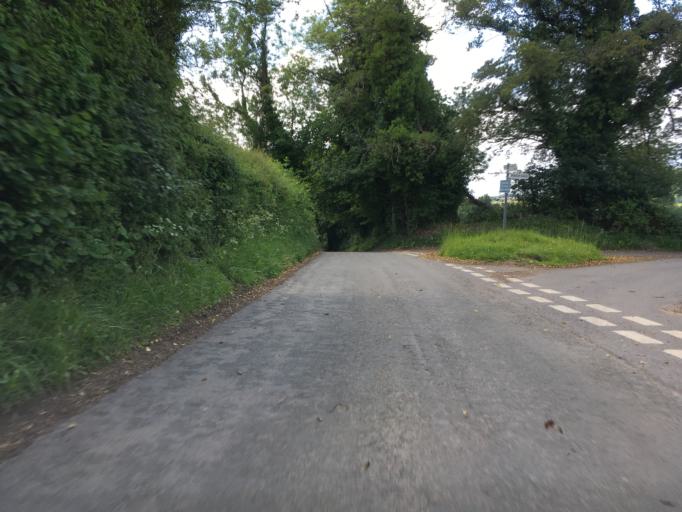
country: GB
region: England
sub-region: Gloucestershire
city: Painswick
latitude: 51.7689
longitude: -2.2003
